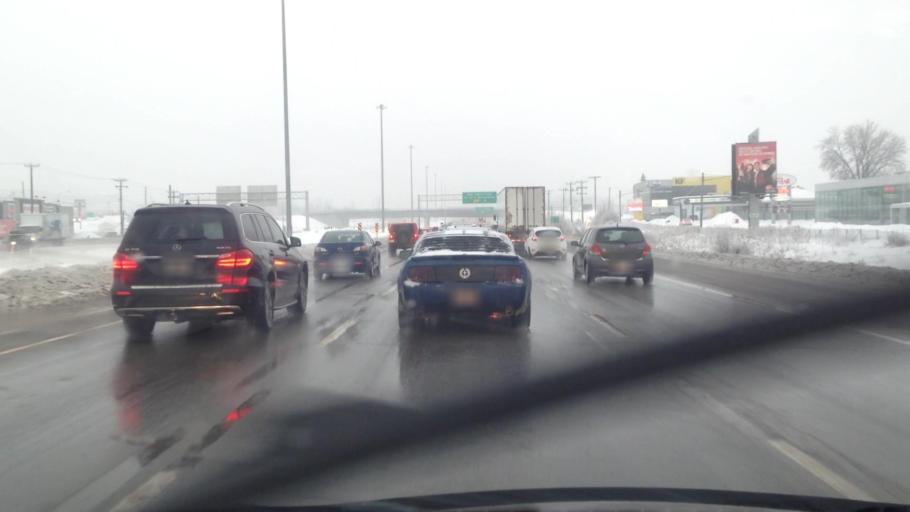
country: CA
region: Quebec
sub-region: Laurentides
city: Boisbriand
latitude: 45.6039
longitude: -73.8059
